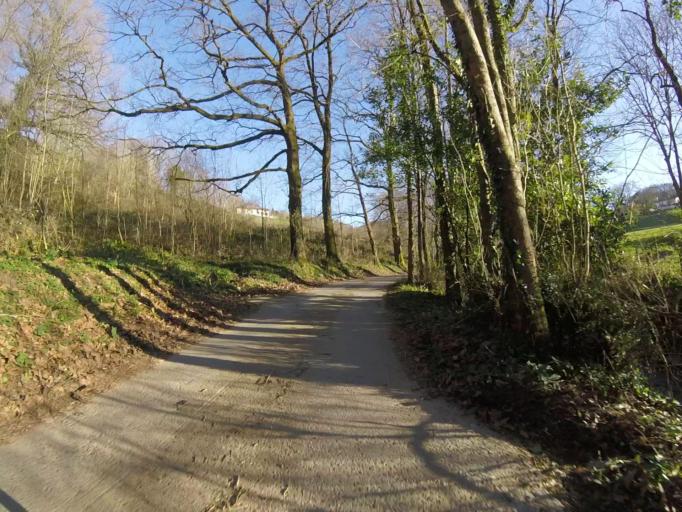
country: ES
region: Basque Country
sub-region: Provincia de Guipuzcoa
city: Errenteria
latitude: 43.2888
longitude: -1.8722
